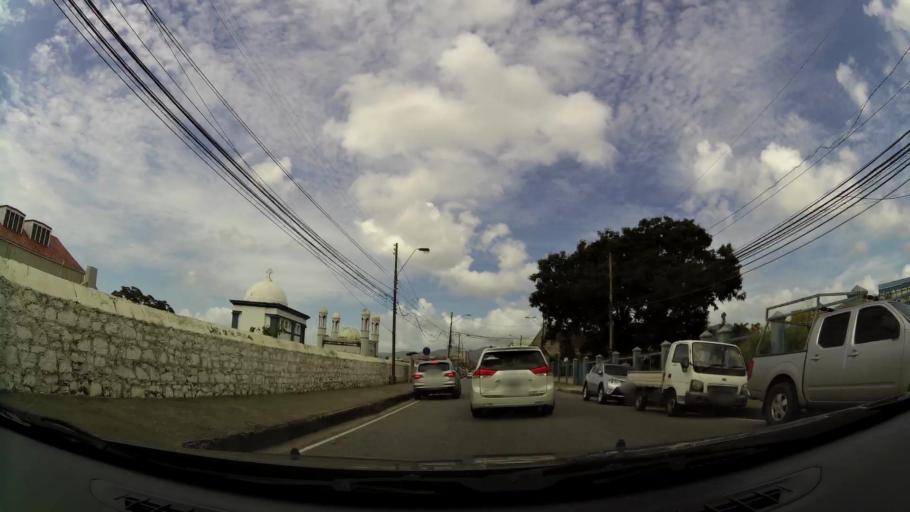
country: TT
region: City of Port of Spain
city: Port-of-Spain
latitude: 10.6587
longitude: -61.5147
